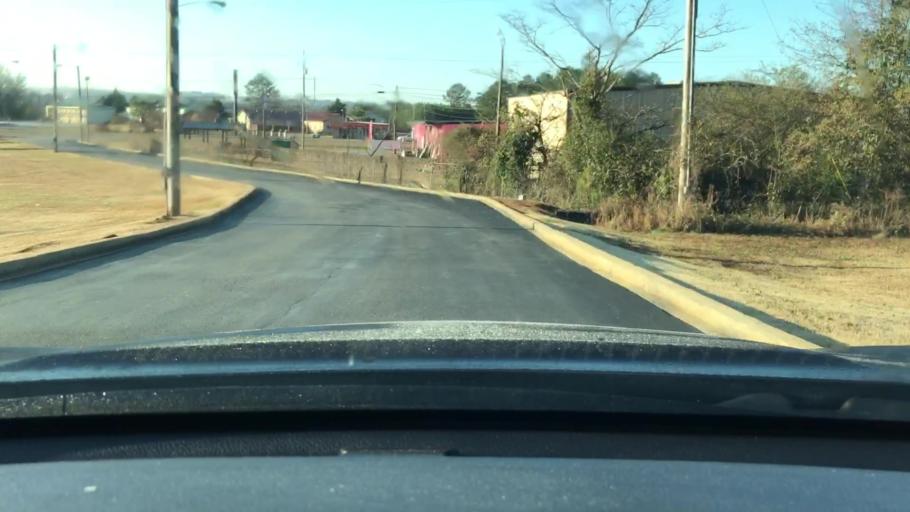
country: US
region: Alabama
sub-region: Talladega County
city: Mignon
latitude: 33.1786
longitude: -86.2930
